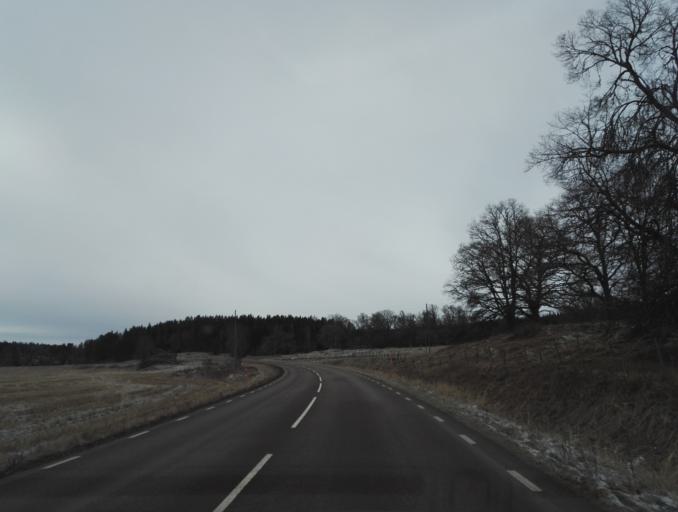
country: SE
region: Kalmar
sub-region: Hultsfreds Kommun
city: Virserum
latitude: 57.3491
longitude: 15.6060
